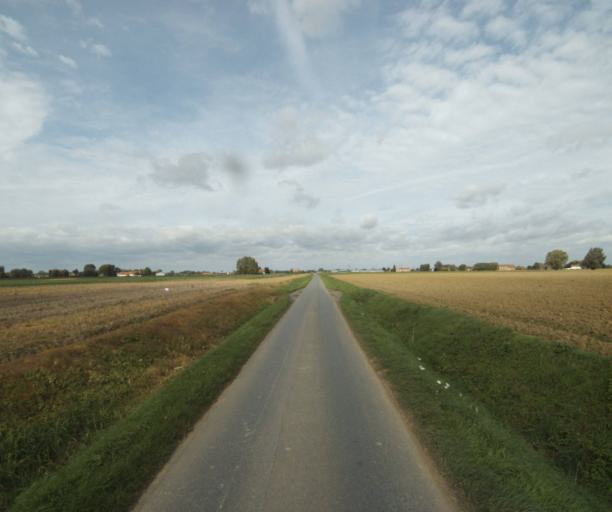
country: FR
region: Nord-Pas-de-Calais
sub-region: Departement du Nord
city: Bois-Grenier
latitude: 50.6421
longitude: 2.8624
